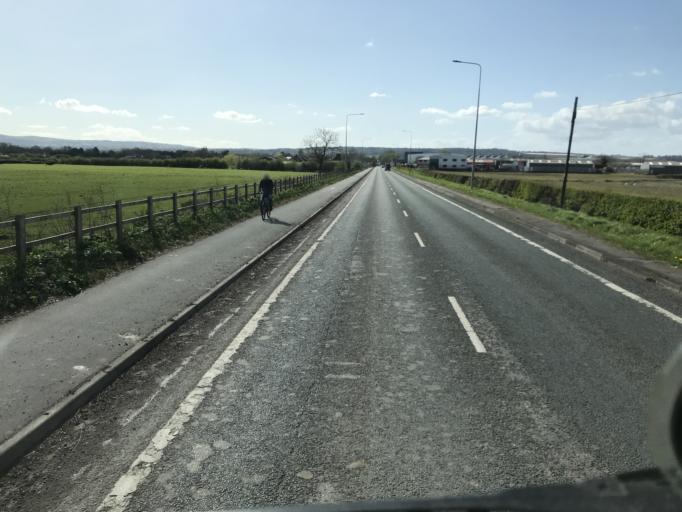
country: GB
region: England
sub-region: Cheshire West and Chester
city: Blacon
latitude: 53.1740
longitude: -2.9558
